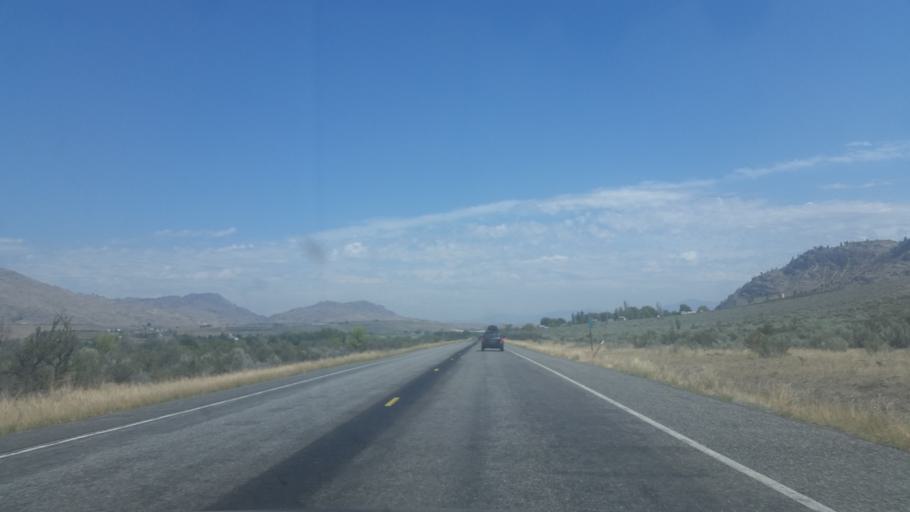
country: US
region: Washington
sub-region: Okanogan County
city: Okanogan
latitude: 48.2720
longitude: -119.7130
